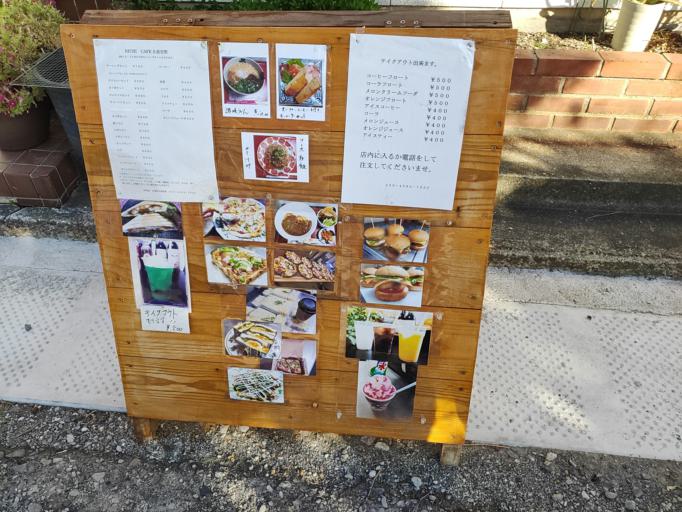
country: JP
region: Nagasaki
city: Fukuecho
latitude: 32.6948
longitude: 128.8487
